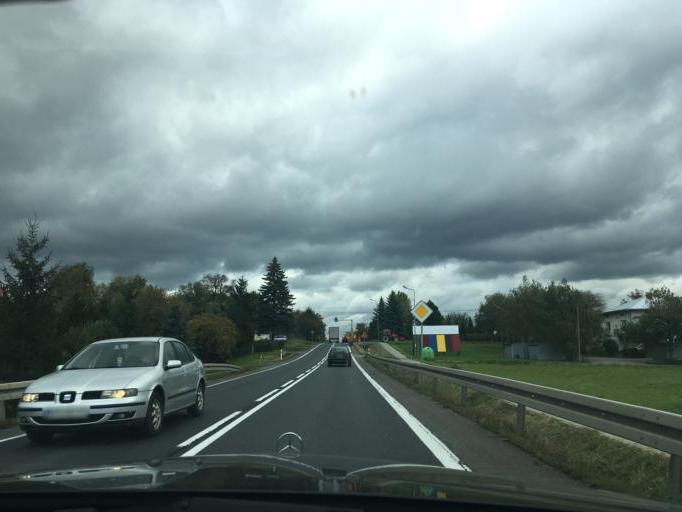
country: PL
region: Subcarpathian Voivodeship
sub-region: Powiat krosnienski
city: Miejsce Piastowe
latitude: 49.6224
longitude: 21.7649
